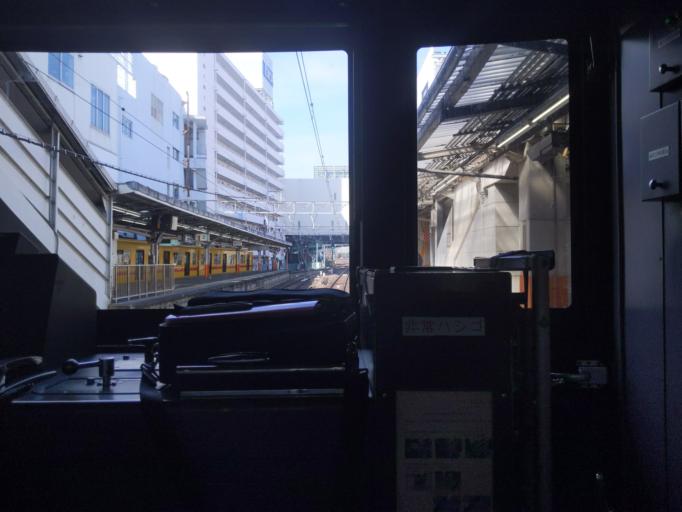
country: JP
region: Saitama
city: Soka
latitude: 35.7772
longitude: 139.7903
